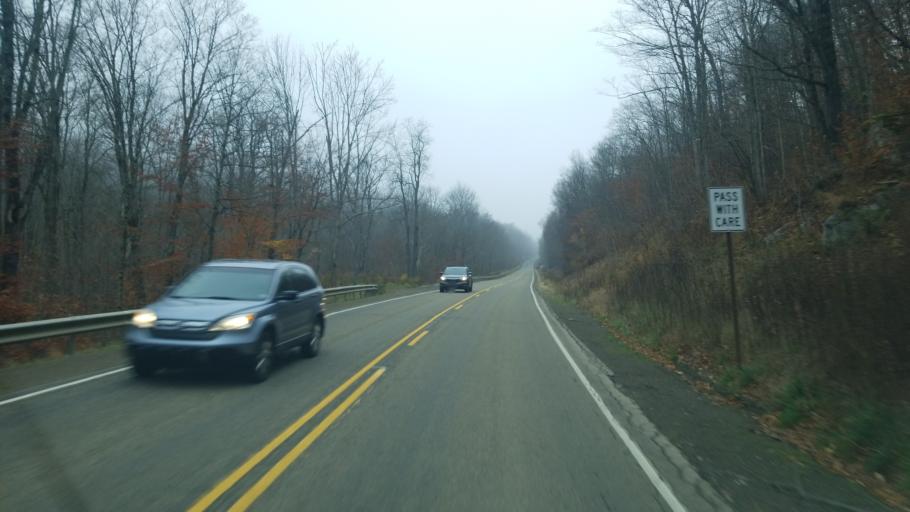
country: US
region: Pennsylvania
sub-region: McKean County
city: Smethport
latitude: 41.8067
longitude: -78.5094
